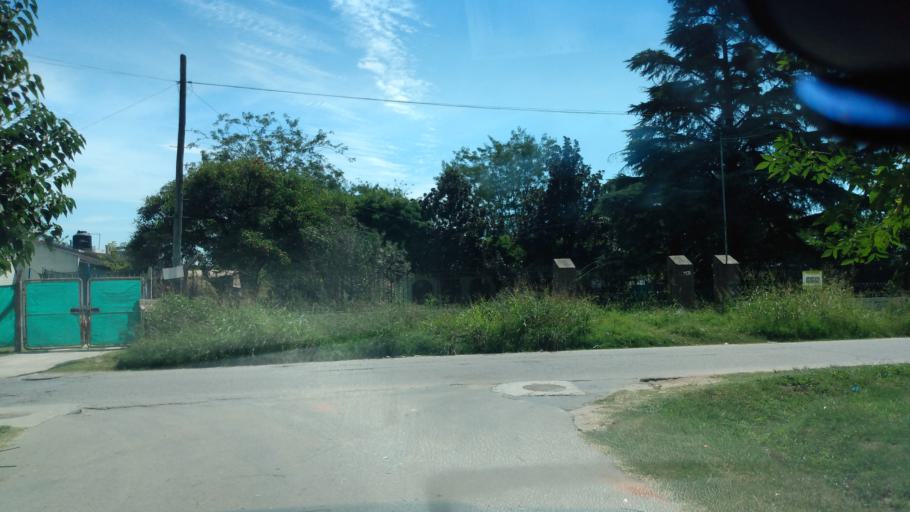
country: AR
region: Buenos Aires
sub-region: Partido de Lujan
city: Lujan
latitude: -34.5513
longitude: -59.1211
